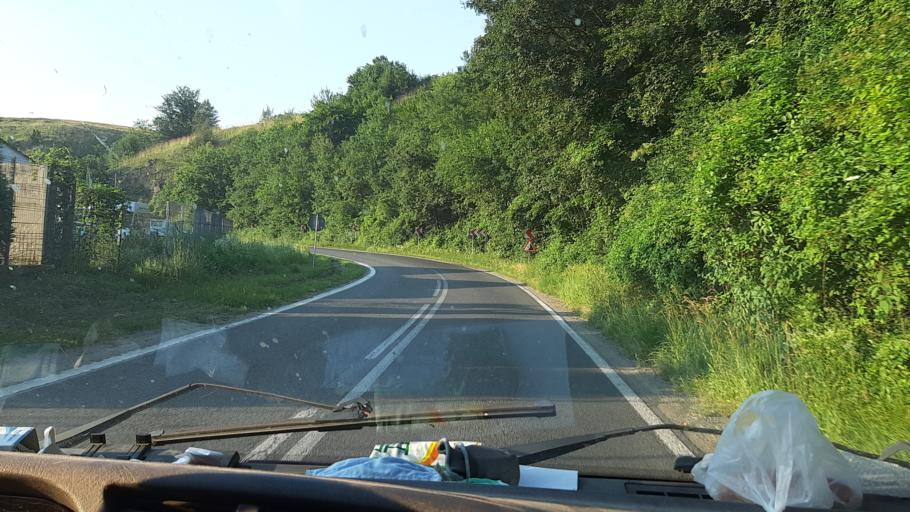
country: RO
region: Caras-Severin
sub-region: Municipiul Resita
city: Calnic
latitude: 45.3487
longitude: 21.8367
